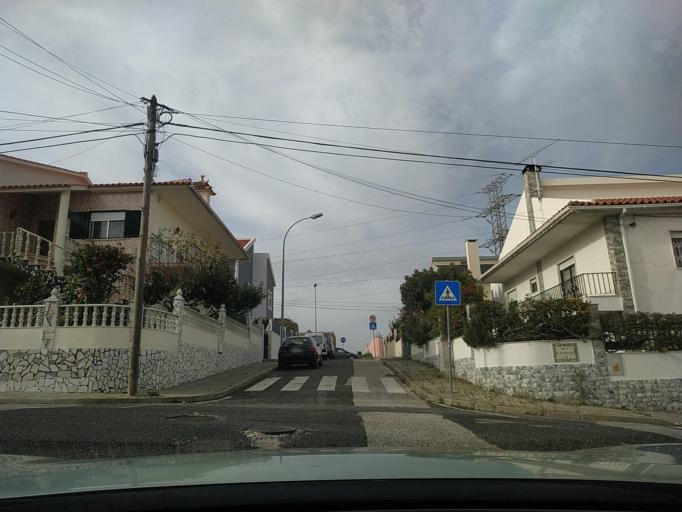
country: PT
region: Lisbon
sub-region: Sintra
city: Belas
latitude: 38.7787
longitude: -9.2429
